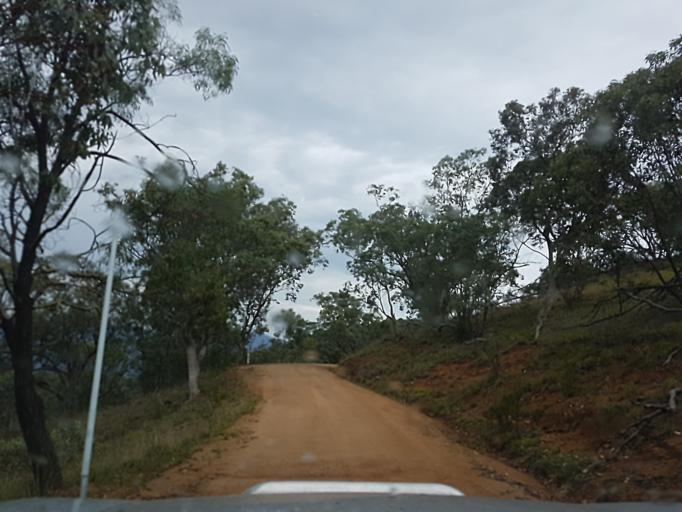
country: AU
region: New South Wales
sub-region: Snowy River
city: Jindabyne
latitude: -36.9476
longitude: 148.3478
